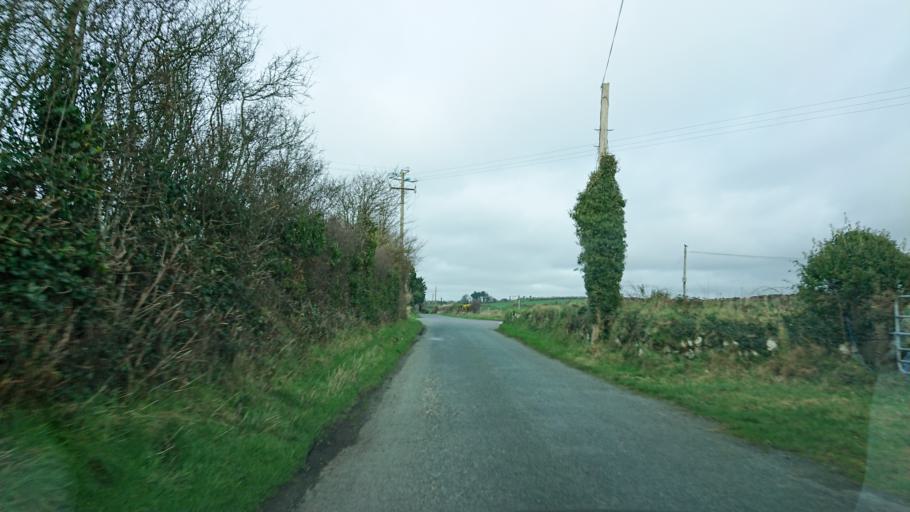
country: IE
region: Munster
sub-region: Waterford
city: Portlaw
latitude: 52.1638
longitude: -7.3057
